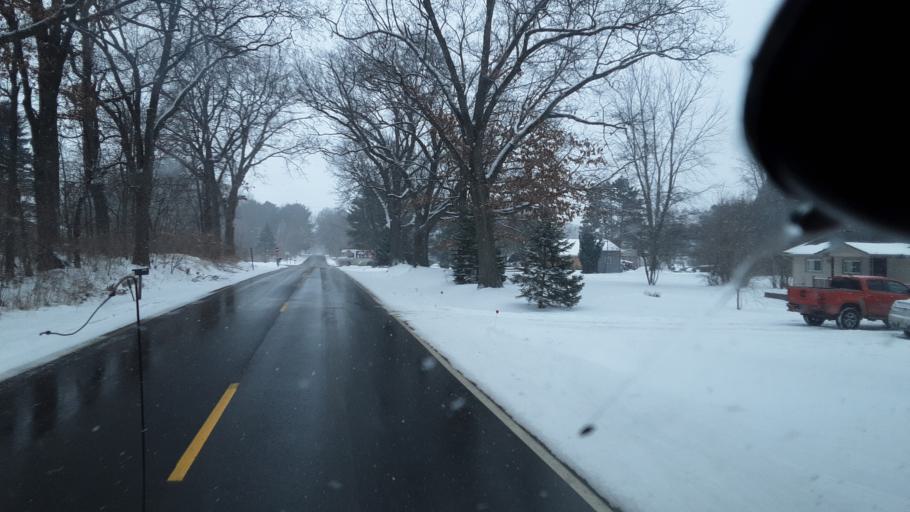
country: US
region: Michigan
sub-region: Ingham County
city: Leslie
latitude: 42.3800
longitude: -84.4432
